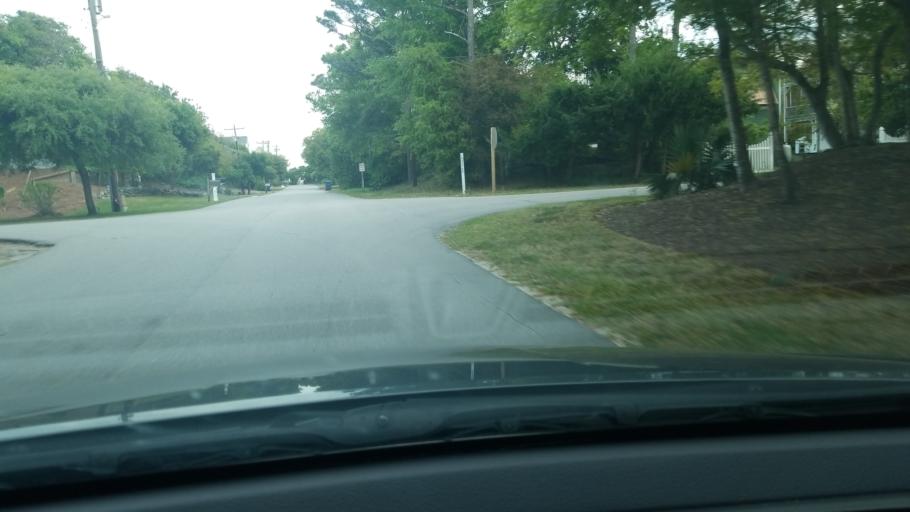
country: US
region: North Carolina
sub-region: Carteret County
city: Cape Carteret
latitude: 34.6675
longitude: -77.0169
